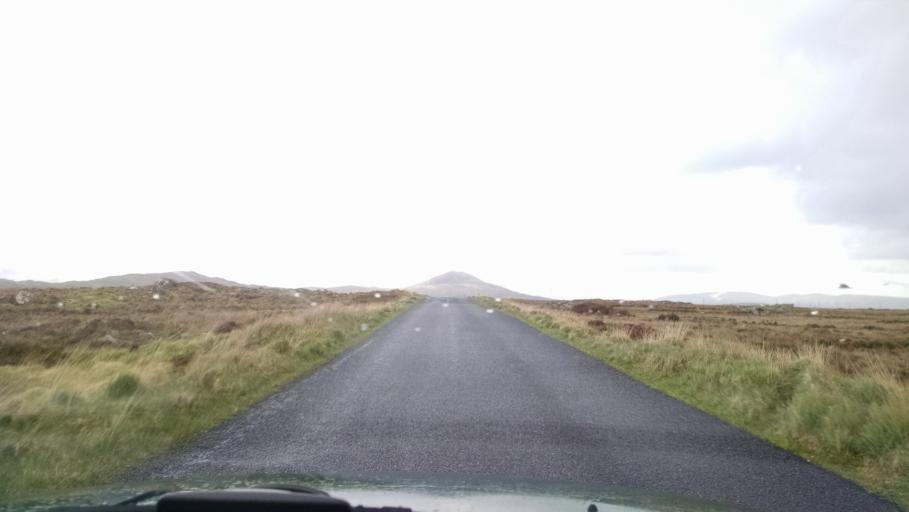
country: IE
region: Connaught
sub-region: County Galway
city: Clifden
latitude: 53.4345
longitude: -9.8999
